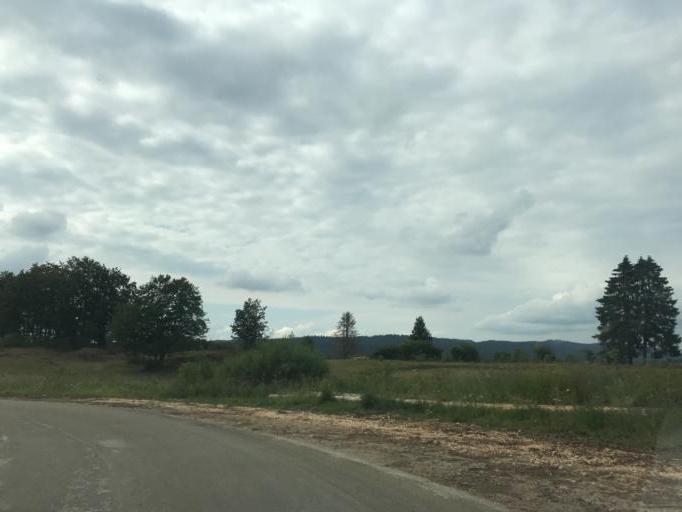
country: FR
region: Franche-Comte
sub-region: Departement du Jura
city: Longchaumois
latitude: 46.5095
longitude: 5.8865
